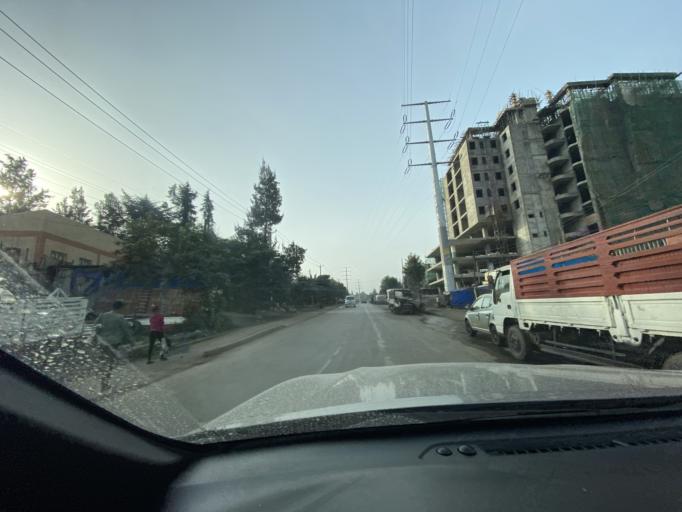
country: ET
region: Adis Abeba
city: Addis Ababa
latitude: 9.0182
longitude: 38.7275
